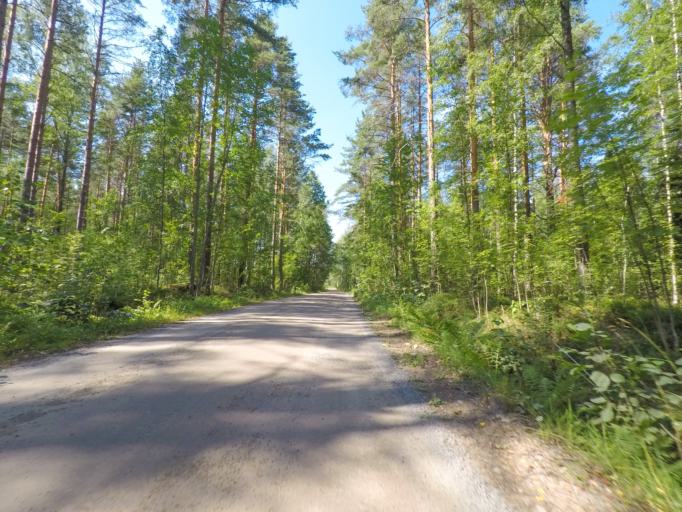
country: FI
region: Southern Savonia
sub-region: Mikkeli
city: Puumala
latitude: 61.4277
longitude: 28.0223
